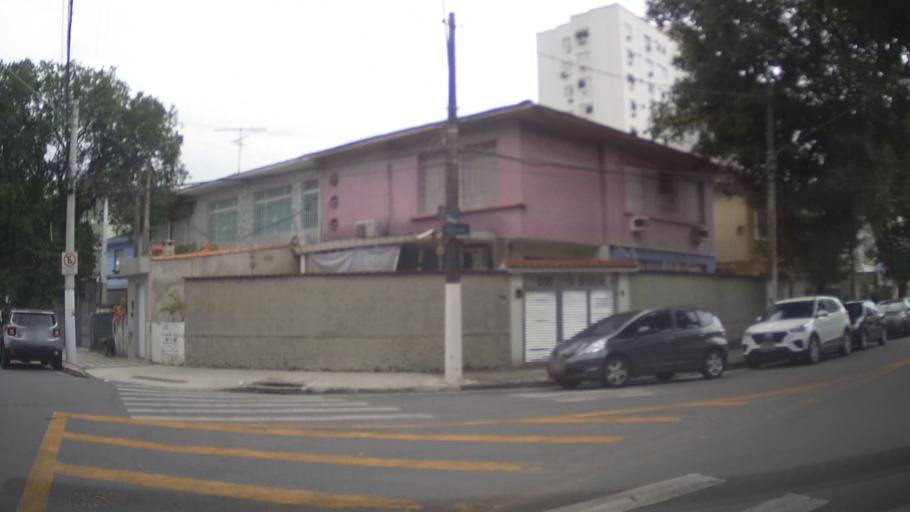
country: BR
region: Sao Paulo
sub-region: Santos
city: Santos
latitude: -23.9558
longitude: -46.3302
